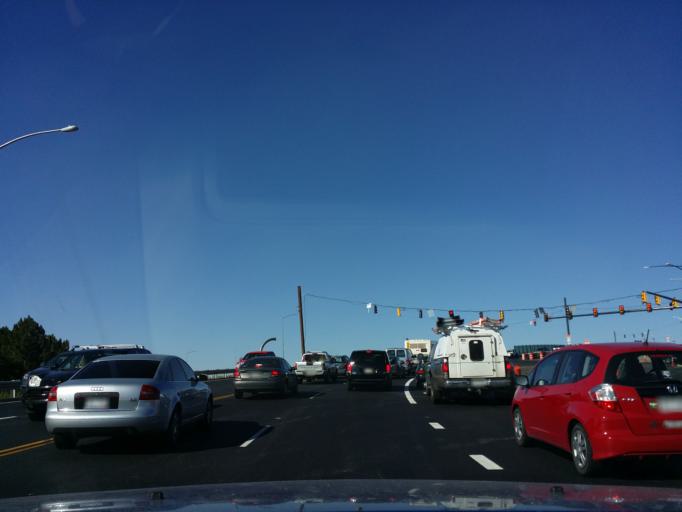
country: US
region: Colorado
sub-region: Adams County
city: Westminster
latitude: 39.8585
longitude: -105.0558
